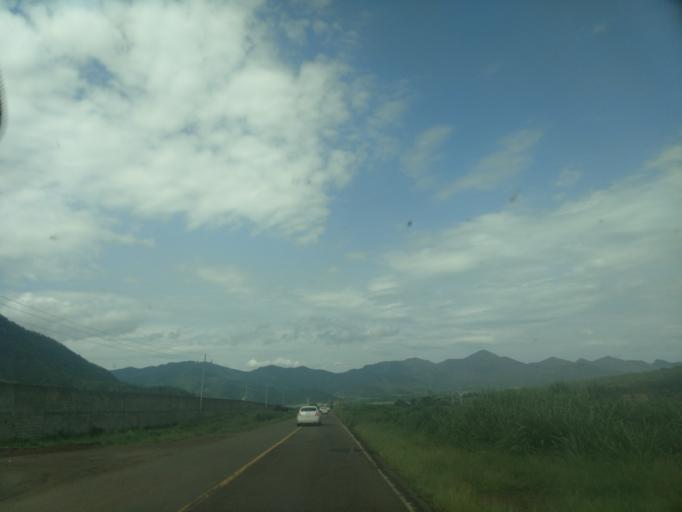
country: MX
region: Jalisco
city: Talpa de Allende
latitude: 20.4216
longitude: -104.7215
